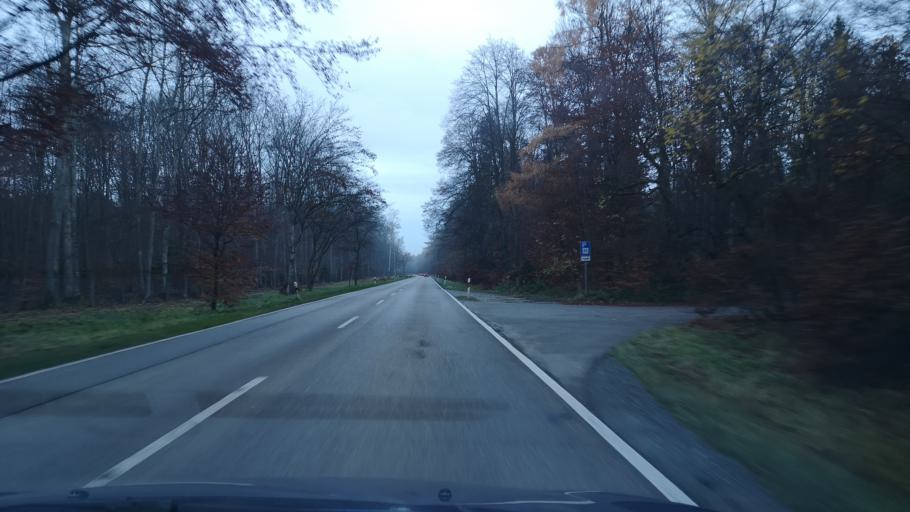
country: DE
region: Bavaria
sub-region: Upper Bavaria
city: Ebersberg
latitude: 48.1168
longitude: 11.9520
